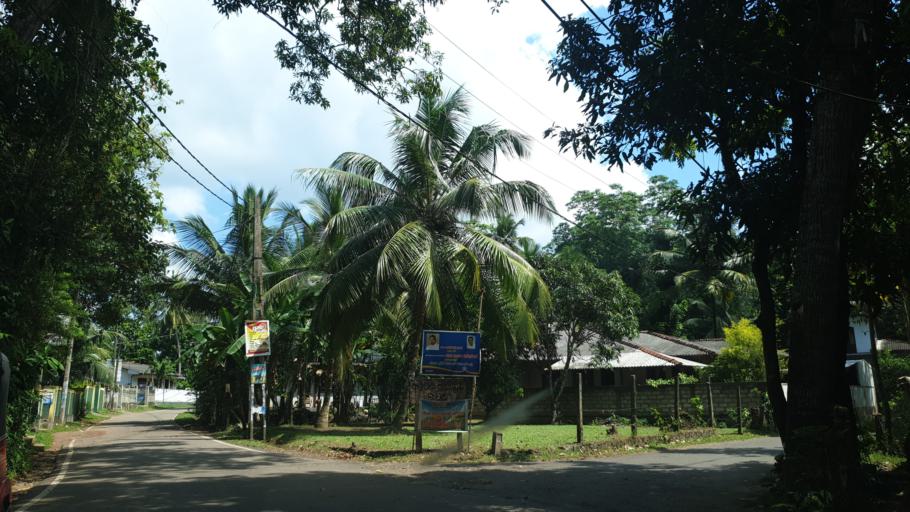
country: LK
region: Western
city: Panadura
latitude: 6.6822
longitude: 79.9418
